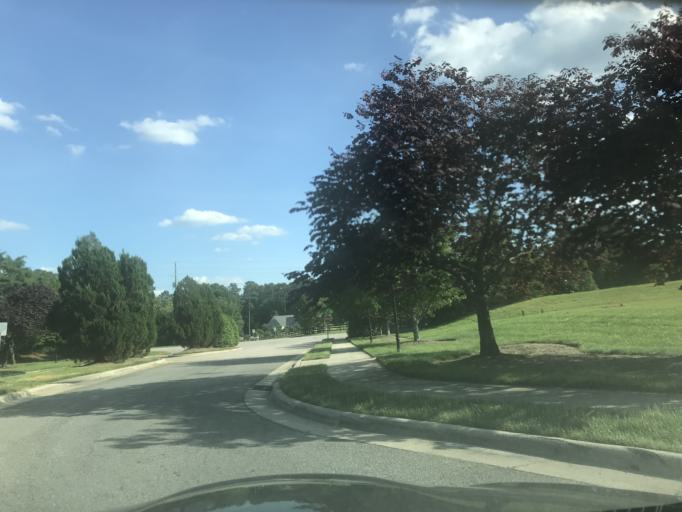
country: US
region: North Carolina
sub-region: Wake County
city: Knightdale
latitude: 35.8350
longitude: -78.5492
